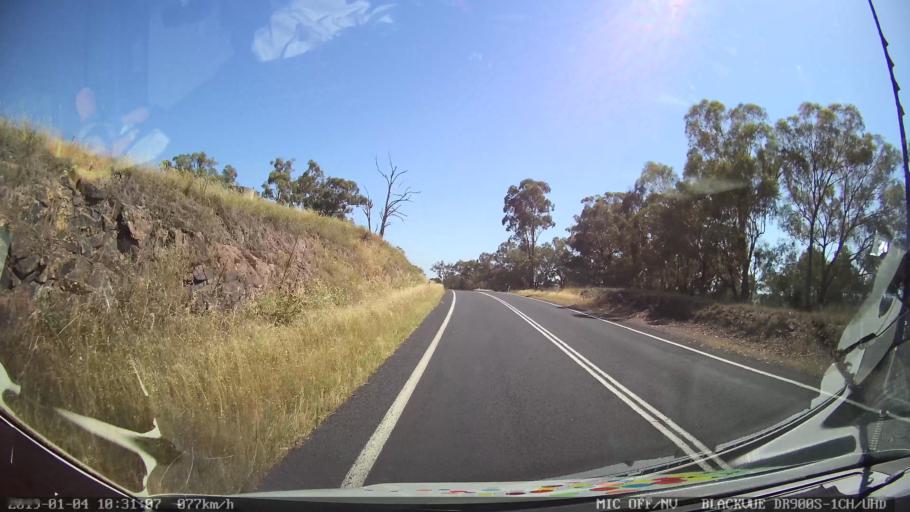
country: AU
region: New South Wales
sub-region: Cabonne
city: Canowindra
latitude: -33.3383
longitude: 148.6314
